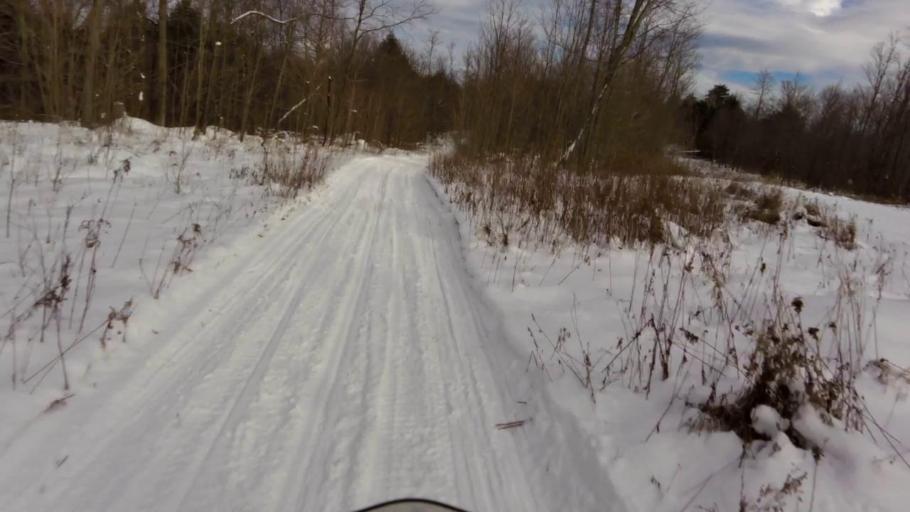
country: US
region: Pennsylvania
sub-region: McKean County
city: Foster Brook
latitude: 42.0101
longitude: -78.5655
